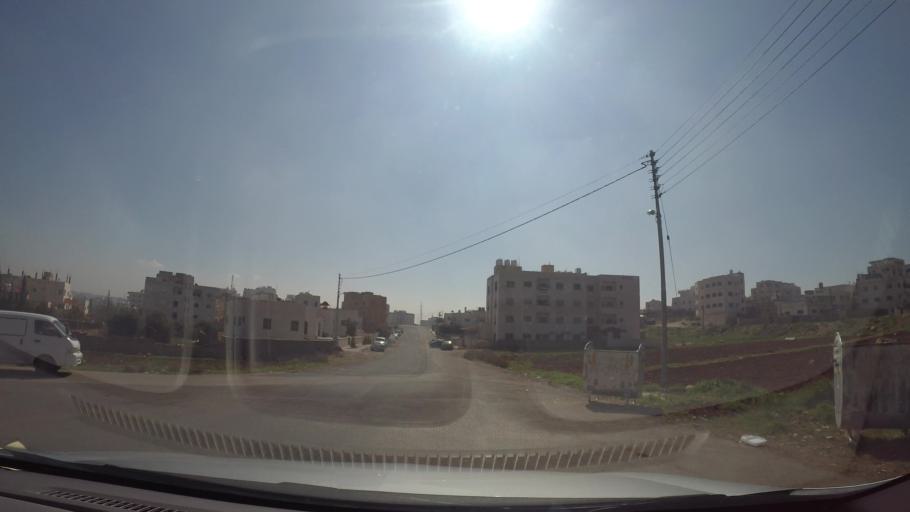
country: JO
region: Amman
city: Al Bunayyat ash Shamaliyah
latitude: 31.8946
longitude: 35.8955
